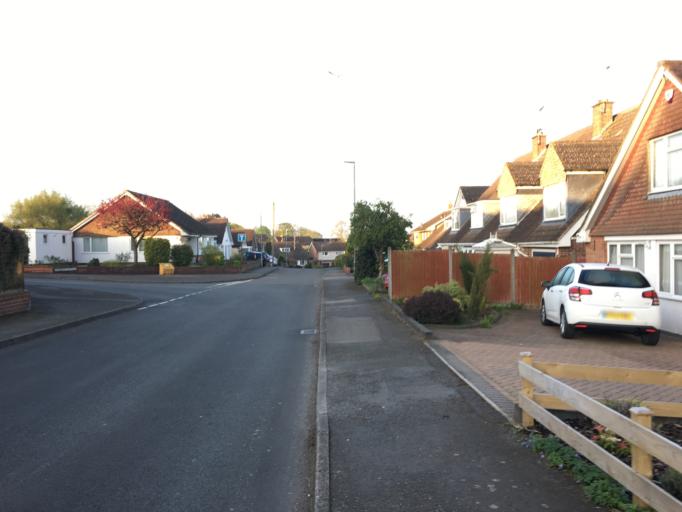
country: GB
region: England
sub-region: Leicestershire
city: Houghton on the Hill
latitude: 52.6284
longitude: -1.0024
